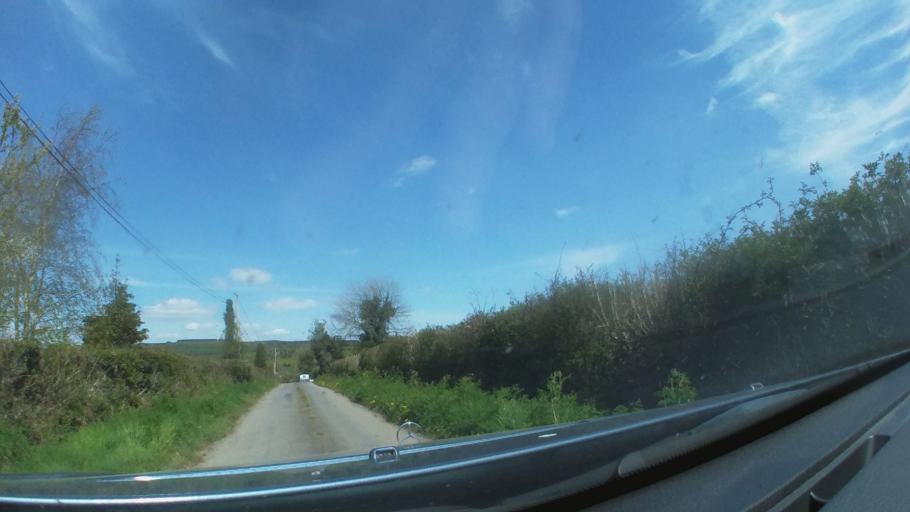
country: IE
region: Leinster
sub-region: Kilkenny
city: Callan
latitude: 52.6208
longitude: -7.4872
